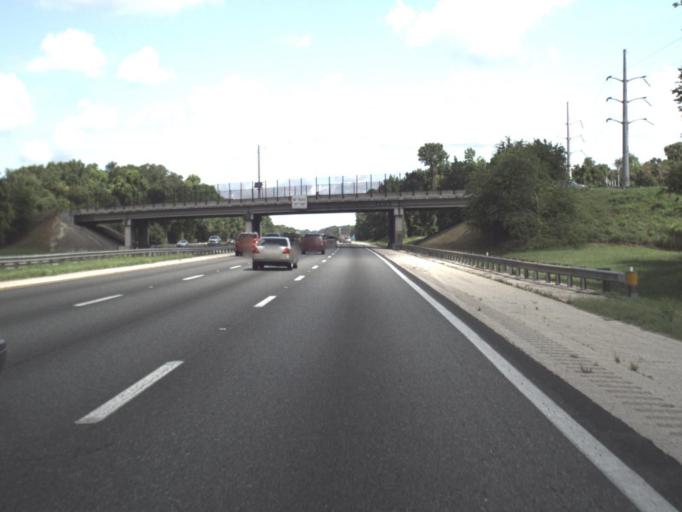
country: US
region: Florida
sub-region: Alachua County
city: Gainesville
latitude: 29.6389
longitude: -82.4012
